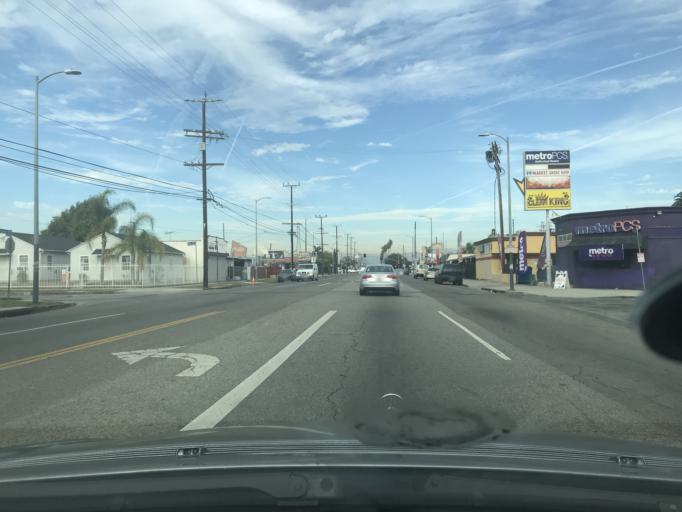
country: US
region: California
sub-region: Los Angeles County
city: Westmont
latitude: 33.9434
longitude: -118.2826
